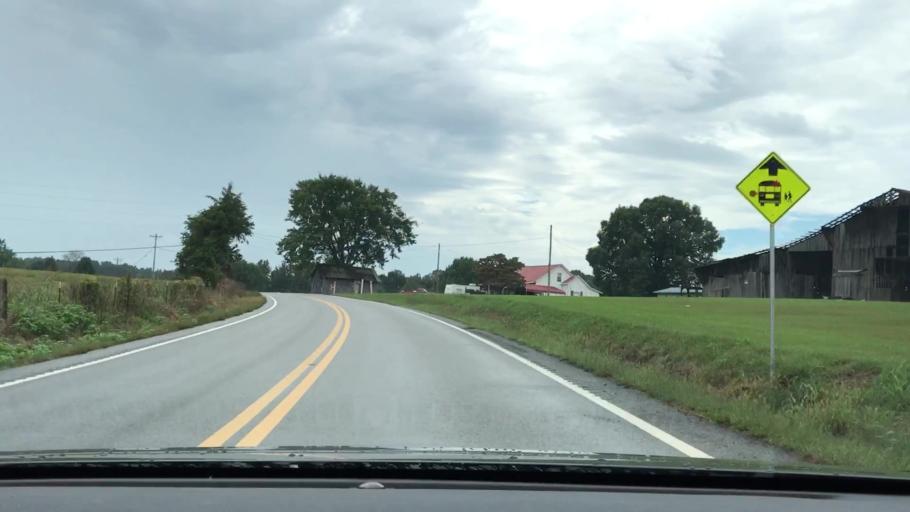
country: US
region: Tennessee
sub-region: Macon County
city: Red Boiling Springs
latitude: 36.5594
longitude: -85.8018
